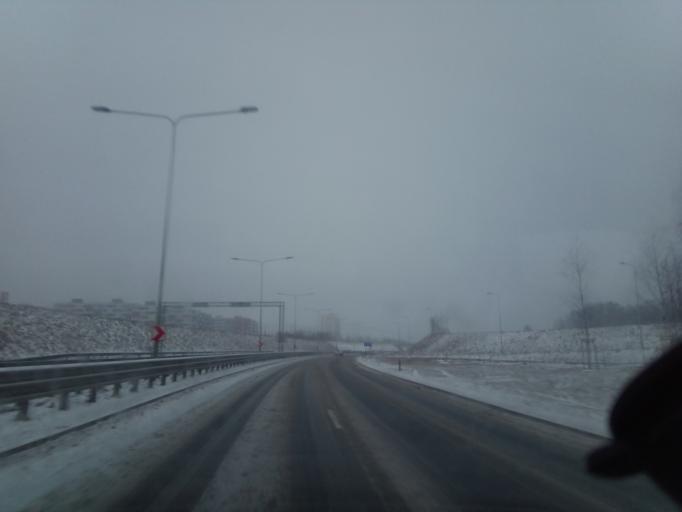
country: LT
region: Vilnius County
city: Pasilaiciai
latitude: 54.7430
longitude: 25.2176
